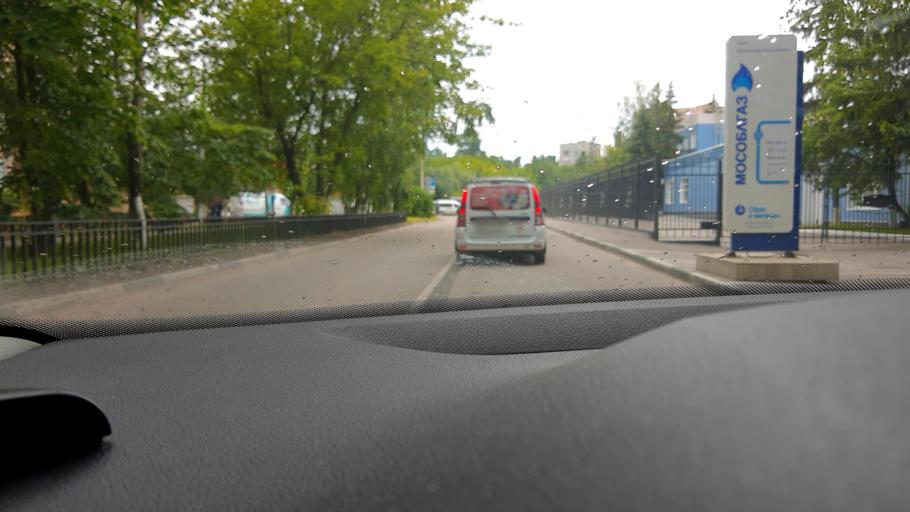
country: RU
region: Moskovskaya
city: Krasnogorsk
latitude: 55.8100
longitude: 37.3243
